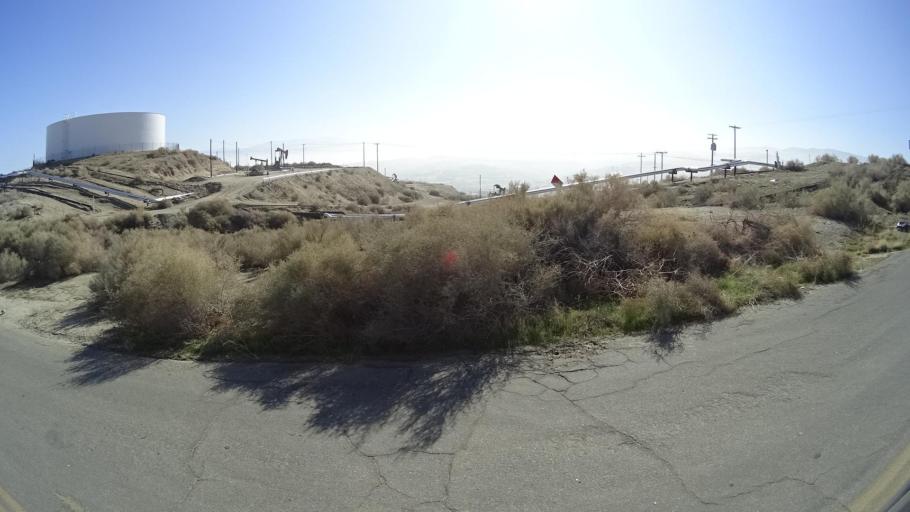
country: US
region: California
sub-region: Kern County
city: Taft Heights
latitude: 35.1144
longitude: -119.4655
